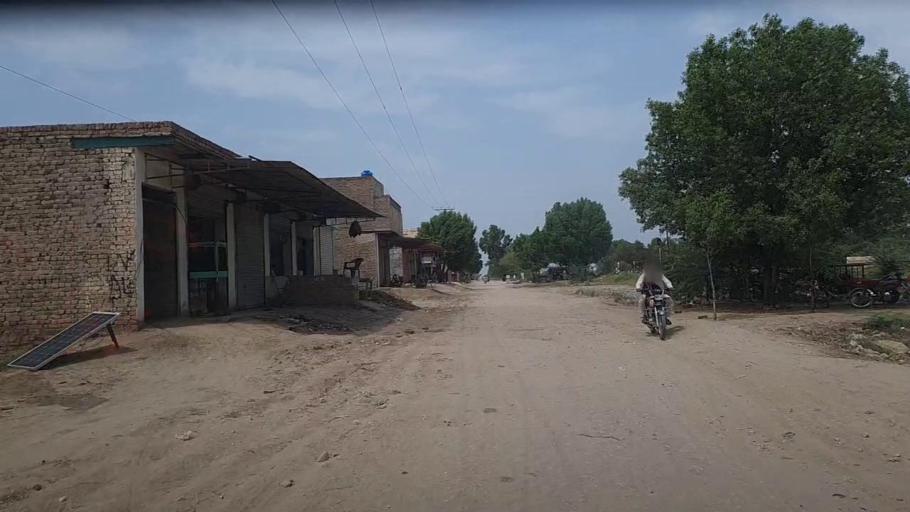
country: PK
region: Sindh
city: Bhiria
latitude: 26.8947
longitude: 68.2860
